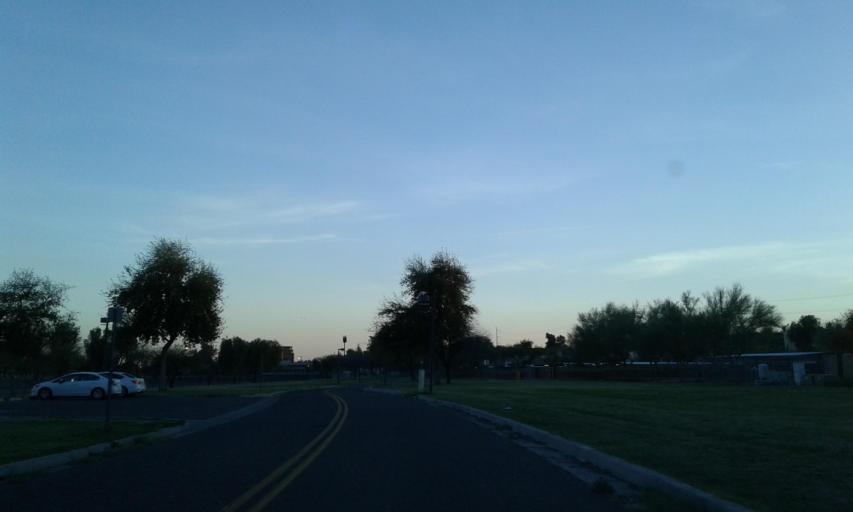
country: US
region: Arizona
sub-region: Maricopa County
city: Glendale
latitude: 33.5931
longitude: -112.1141
